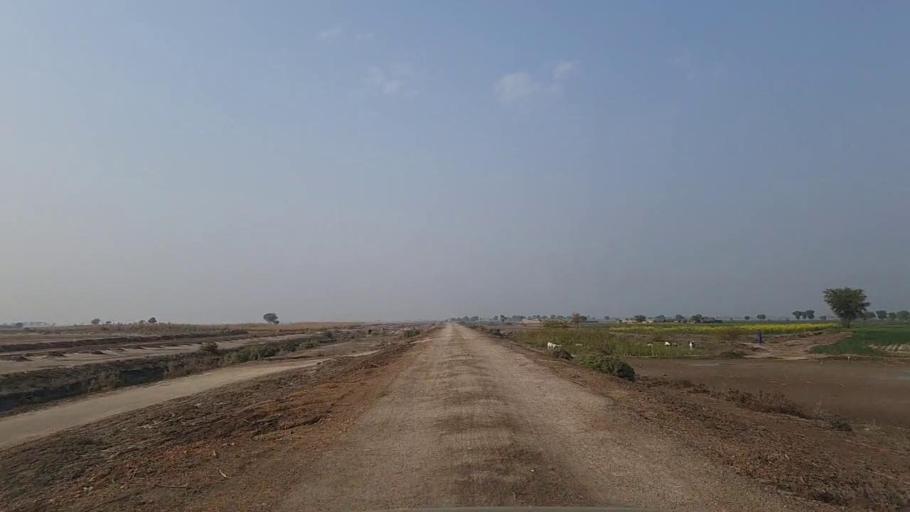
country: PK
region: Sindh
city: Nawabshah
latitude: 26.3305
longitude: 68.4763
